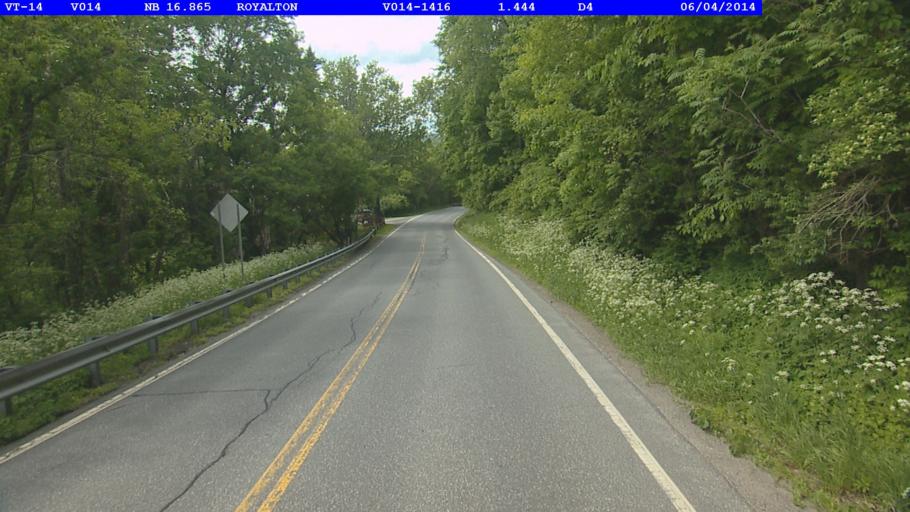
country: US
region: Vermont
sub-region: Orange County
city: Chelsea
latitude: 43.8138
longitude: -72.5075
